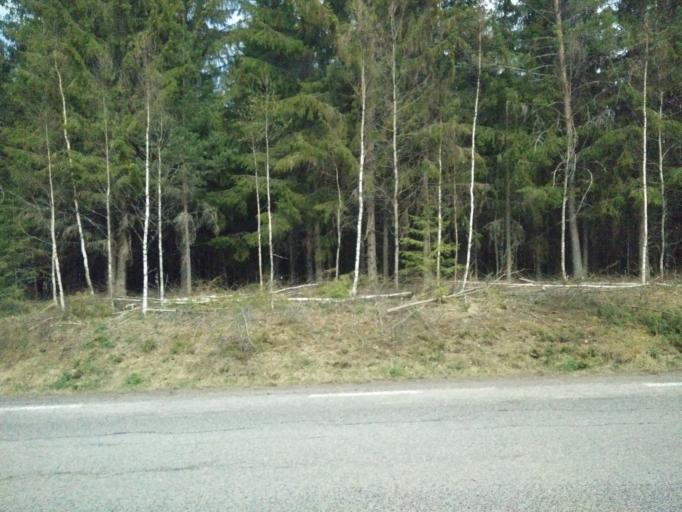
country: SE
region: Vaermland
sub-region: Munkfors Kommun
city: Munkfors
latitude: 59.8362
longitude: 13.5047
